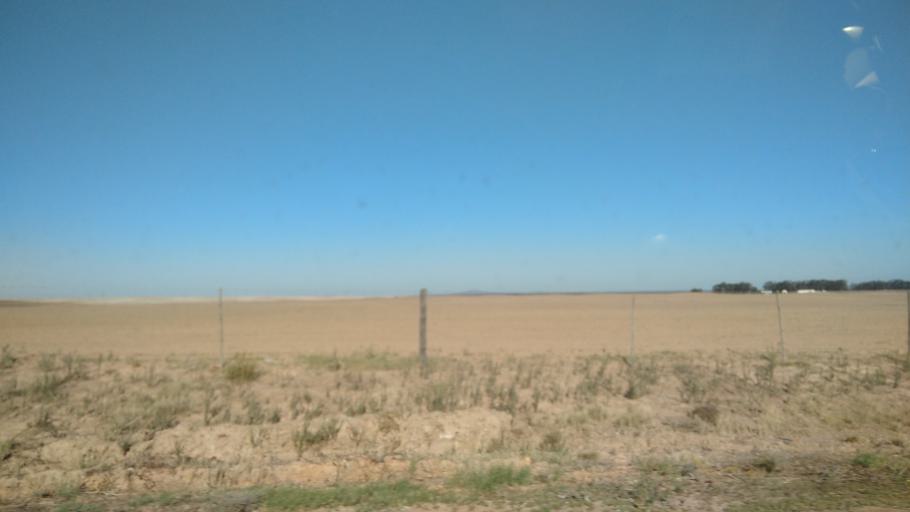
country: ZA
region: Western Cape
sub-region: West Coast District Municipality
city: Moorreesburg
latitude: -33.1386
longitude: 18.4565
